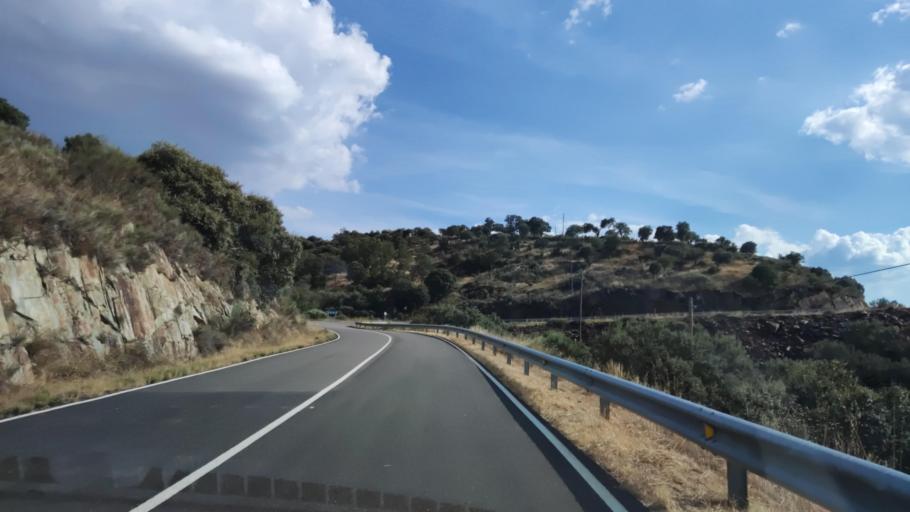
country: ES
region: Castille and Leon
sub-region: Provincia de Salamanca
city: Pastores
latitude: 40.4940
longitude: -6.4953
